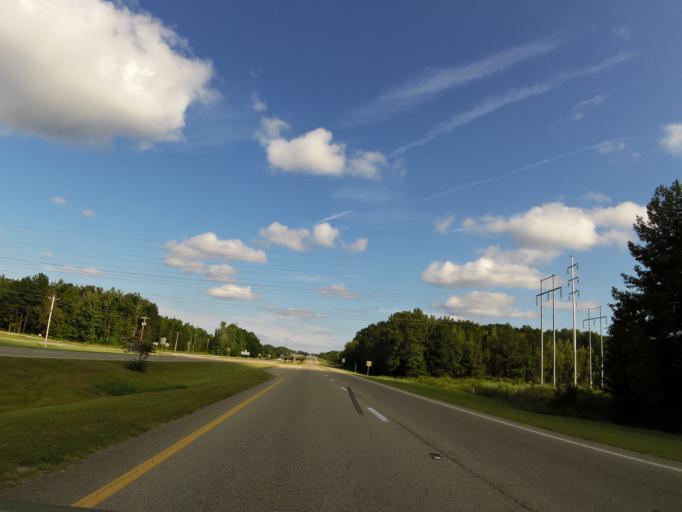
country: US
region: Mississippi
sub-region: Tishomingo County
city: Iuka
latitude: 34.8322
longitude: -88.3111
